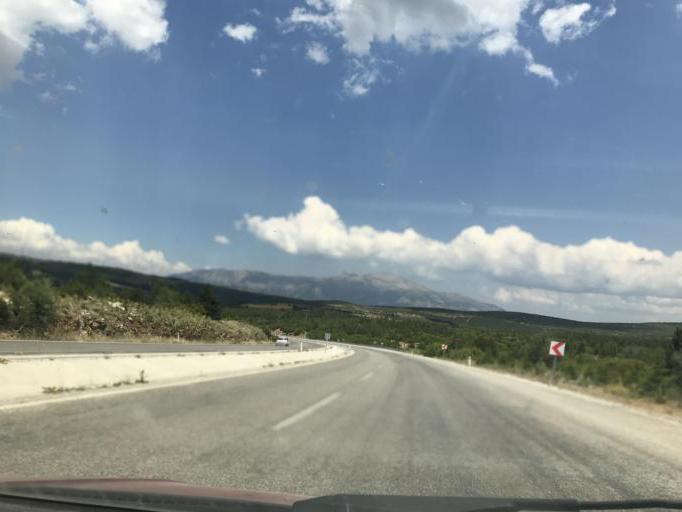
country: TR
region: Denizli
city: Tavas
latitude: 37.5943
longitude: 29.1161
